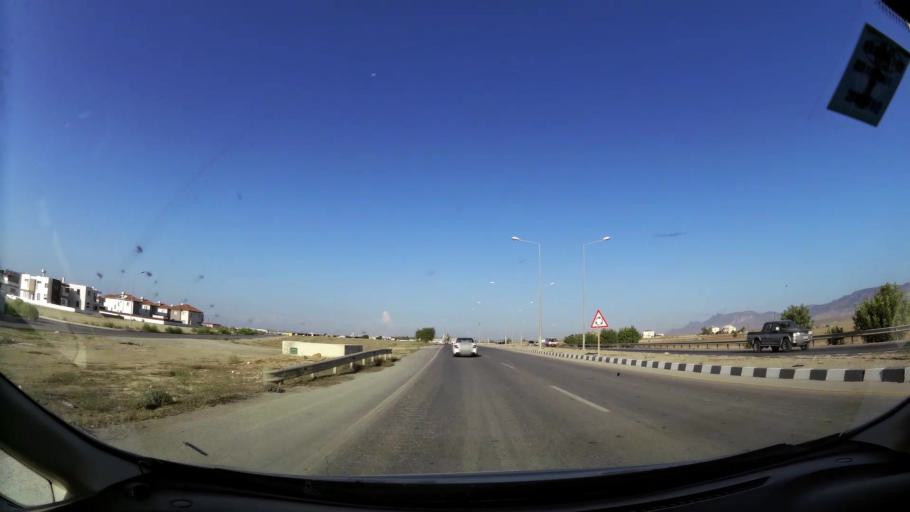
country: CY
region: Lefkosia
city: Nicosia
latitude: 35.2107
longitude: 33.2902
